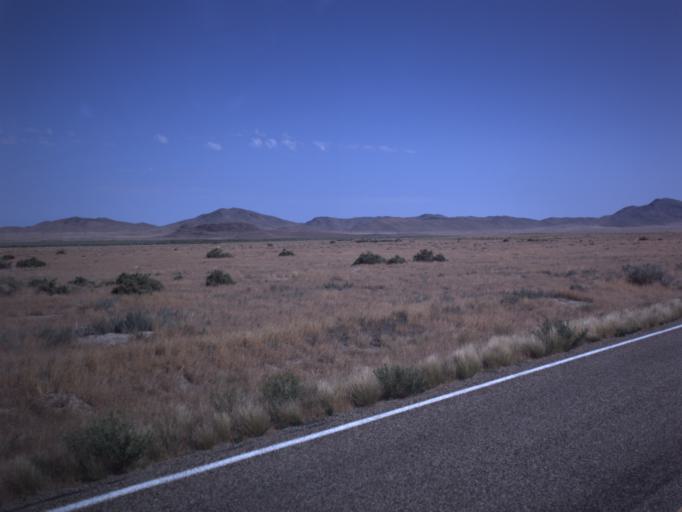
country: US
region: Utah
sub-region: Beaver County
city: Milford
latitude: 38.6533
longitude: -112.9822
